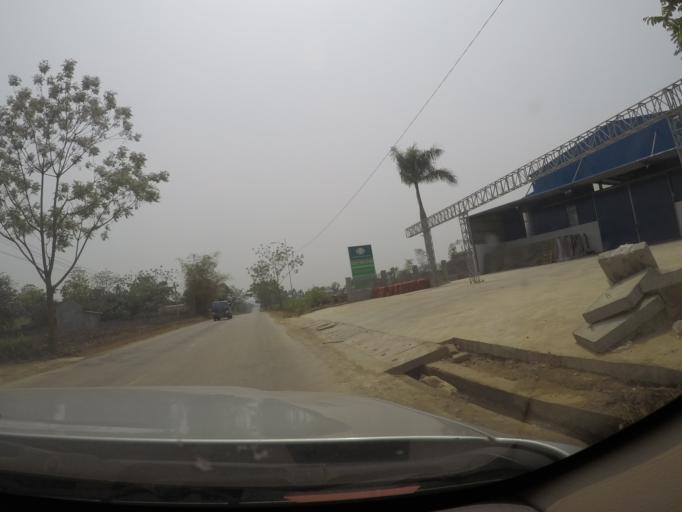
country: VN
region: Thanh Hoa
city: Thi Tran Thuong Xuan
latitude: 19.9336
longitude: 105.3920
